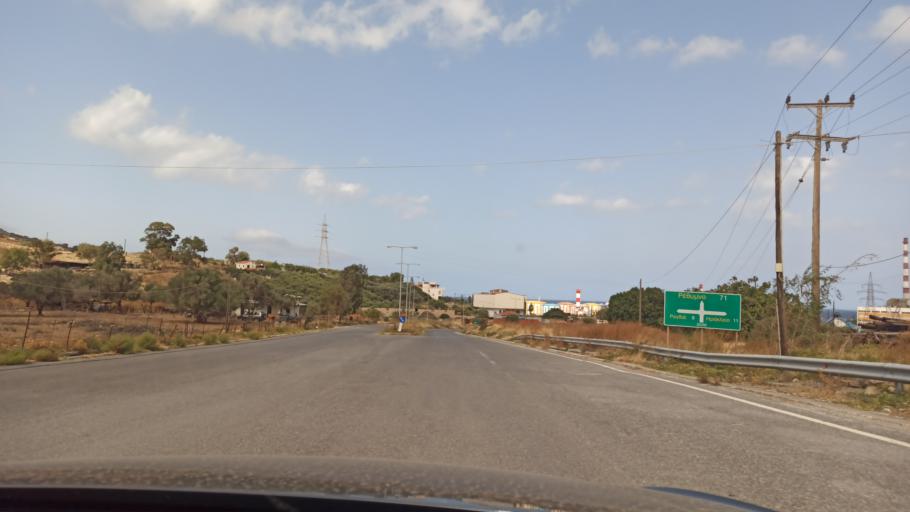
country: GR
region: Crete
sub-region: Nomos Irakleiou
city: Gazi
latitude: 35.3363
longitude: 25.0476
